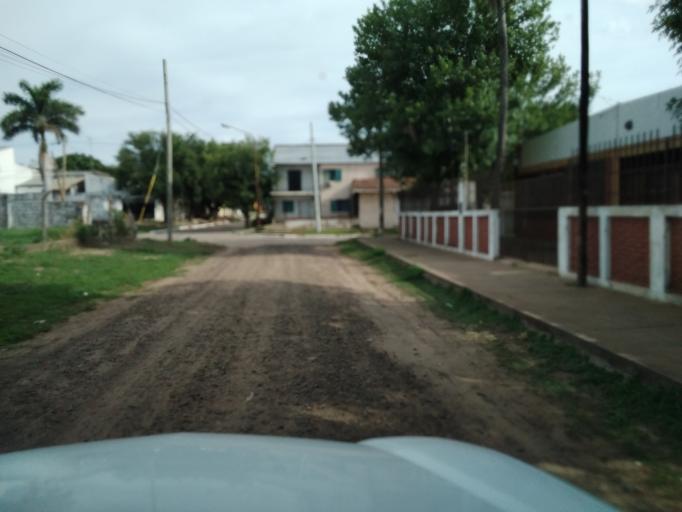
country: AR
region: Corrientes
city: Corrientes
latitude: -27.4829
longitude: -58.8517
